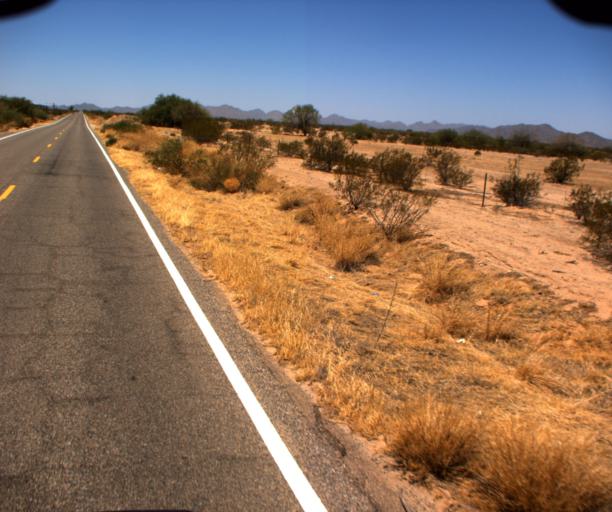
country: US
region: Arizona
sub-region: Pinal County
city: Maricopa
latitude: 33.0495
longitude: -112.2953
